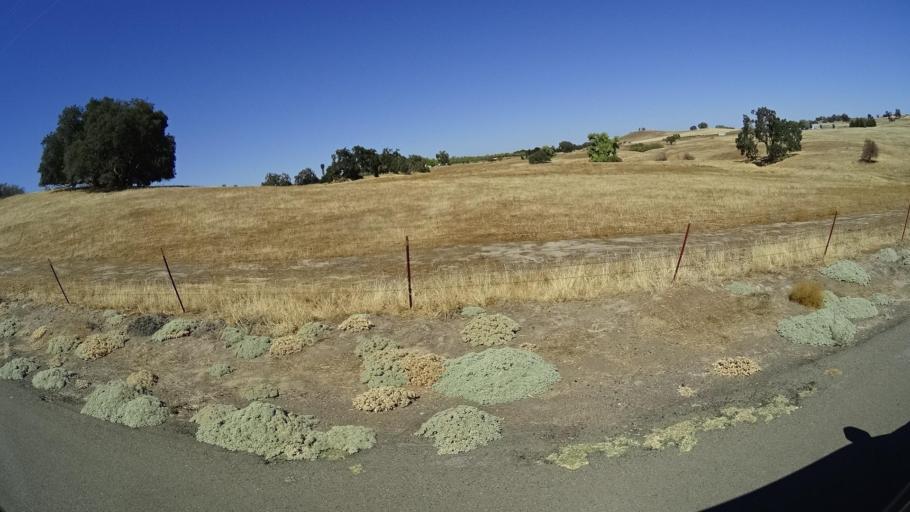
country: US
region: California
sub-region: San Luis Obispo County
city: Lake Nacimiento
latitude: 35.8071
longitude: -121.0544
